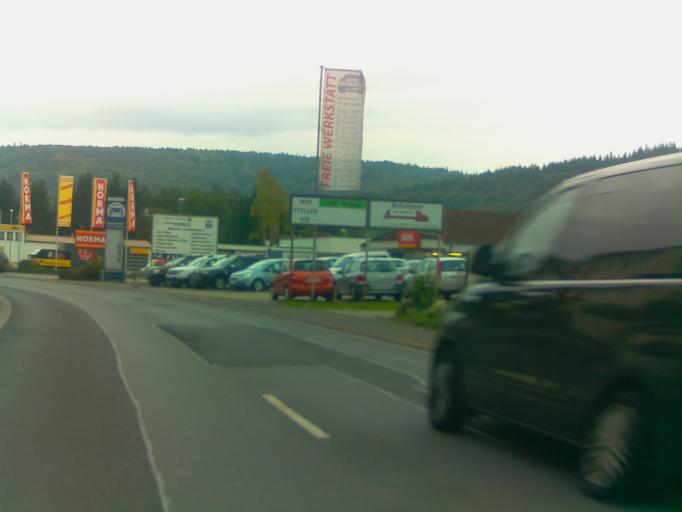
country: DE
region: Bavaria
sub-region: Regierungsbezirk Unterfranken
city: Momlingen
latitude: 49.8509
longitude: 9.0893
